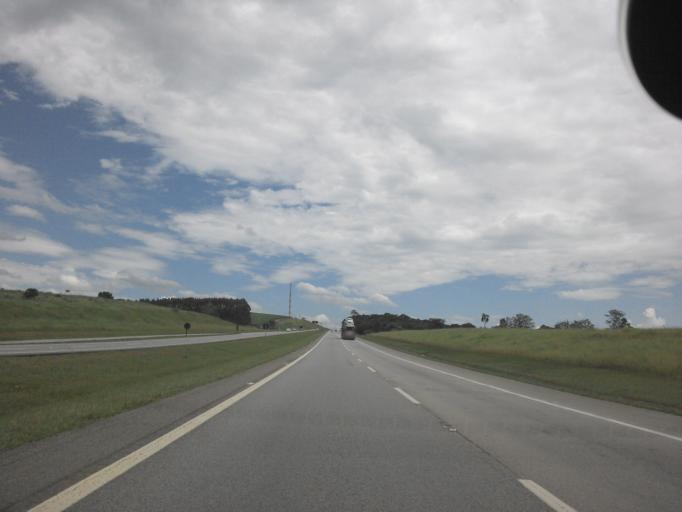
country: BR
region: Sao Paulo
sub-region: Cacapava
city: Cacapava
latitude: -23.1603
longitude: -45.7014
